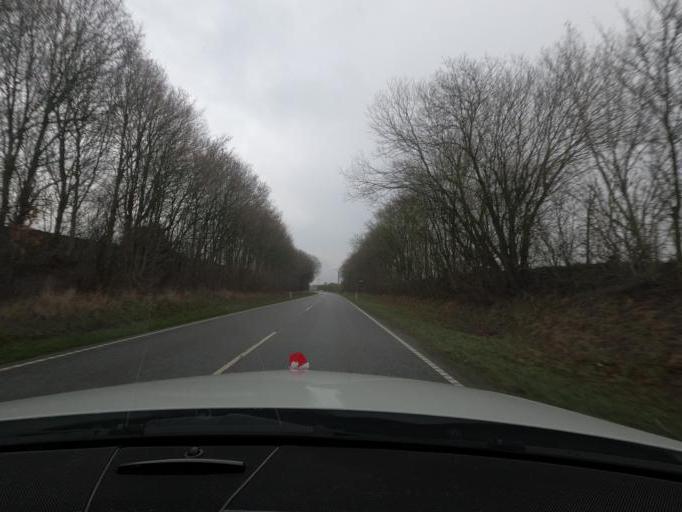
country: DK
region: South Denmark
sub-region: Haderslev Kommune
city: Haderslev
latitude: 55.1992
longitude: 9.4376
